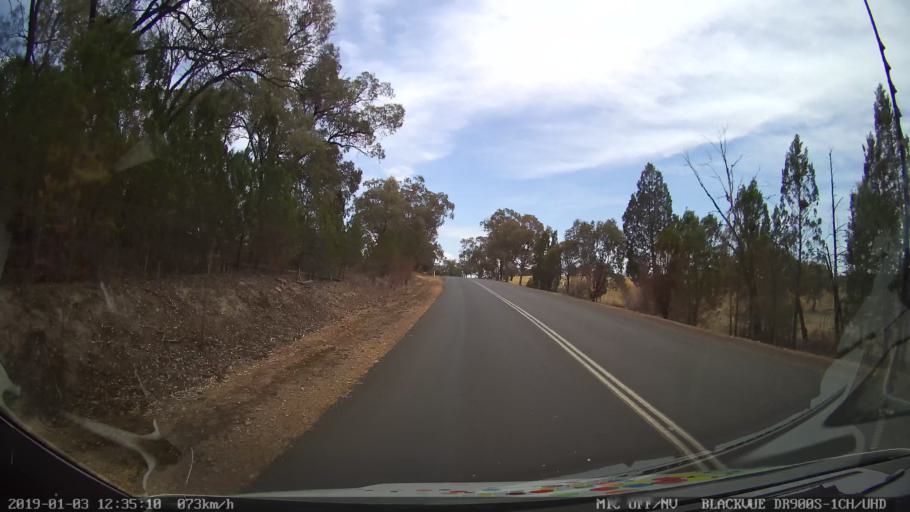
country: AU
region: New South Wales
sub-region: Weddin
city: Grenfell
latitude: -33.8694
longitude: 148.1690
